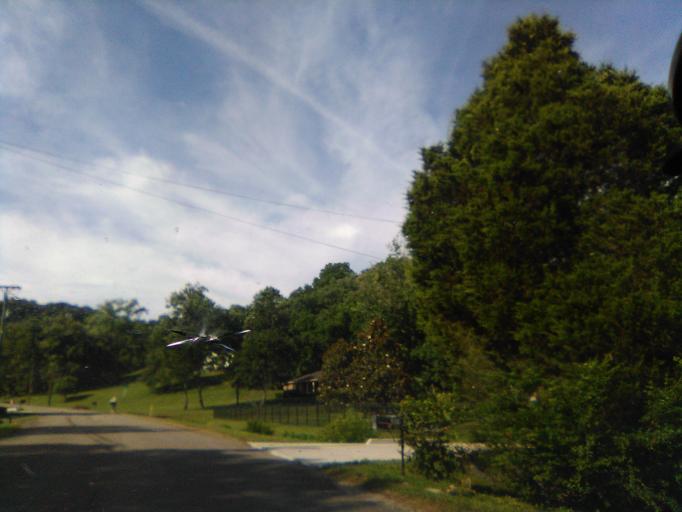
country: US
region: Tennessee
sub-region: Davidson County
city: Belle Meade
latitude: 36.1080
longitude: -86.9112
